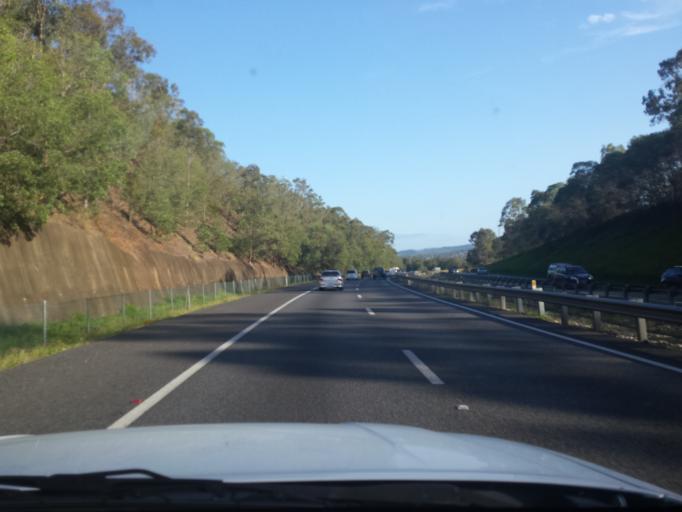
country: AU
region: Queensland
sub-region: Logan
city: Slacks Creek
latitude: -27.6703
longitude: 153.1657
